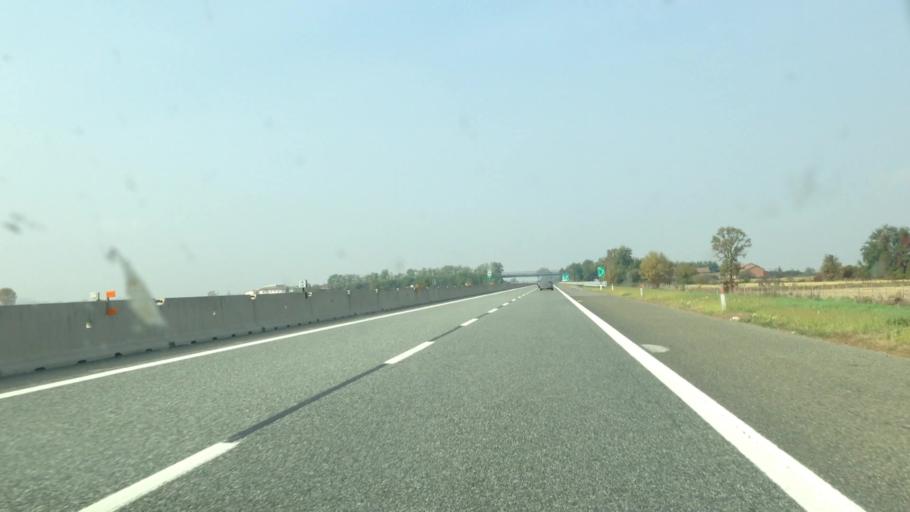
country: IT
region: Piedmont
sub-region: Provincia di Vercelli
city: Sali Vercellese
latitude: 45.3039
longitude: 8.3167
